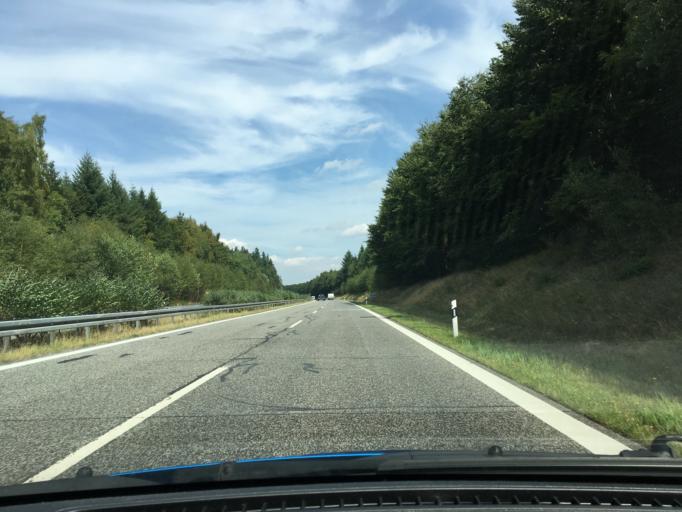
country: DE
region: Mecklenburg-Vorpommern
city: Raben Steinfeld
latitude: 53.5766
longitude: 11.4983
